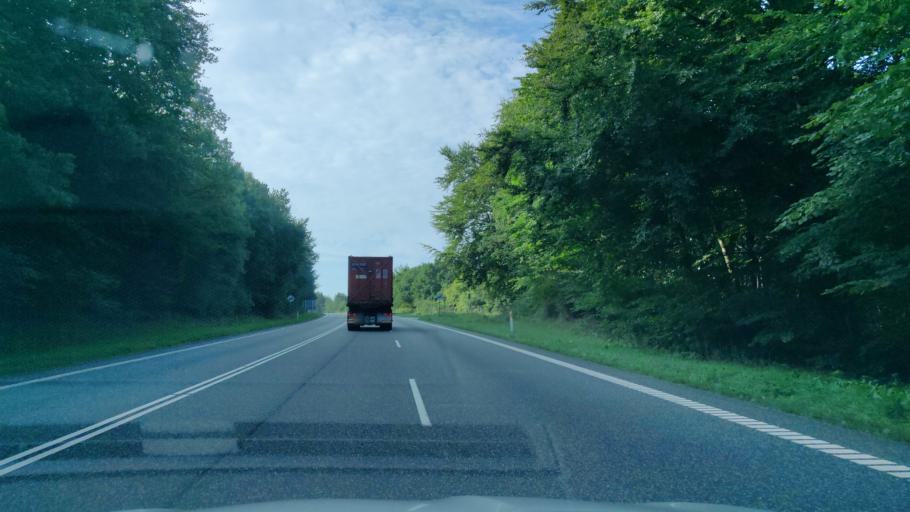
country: DK
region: North Denmark
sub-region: Vesthimmerland Kommune
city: Alestrup
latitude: 56.7342
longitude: 9.5336
